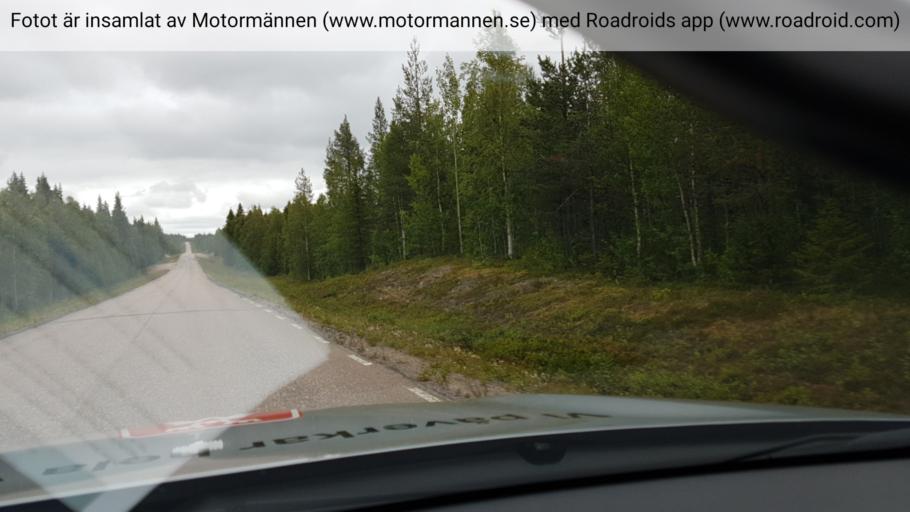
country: SE
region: Norrbotten
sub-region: Overkalix Kommun
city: OEverkalix
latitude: 67.0324
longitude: 22.0176
